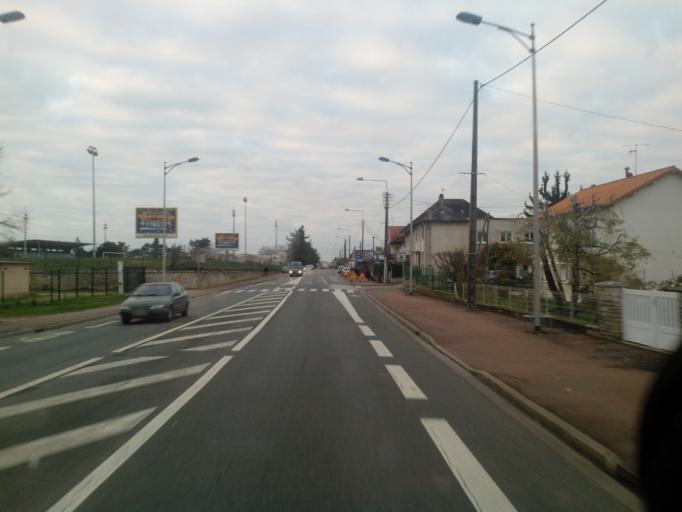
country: FR
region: Poitou-Charentes
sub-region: Departement de la Vienne
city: Saint-Benoit
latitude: 46.5706
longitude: 0.3765
